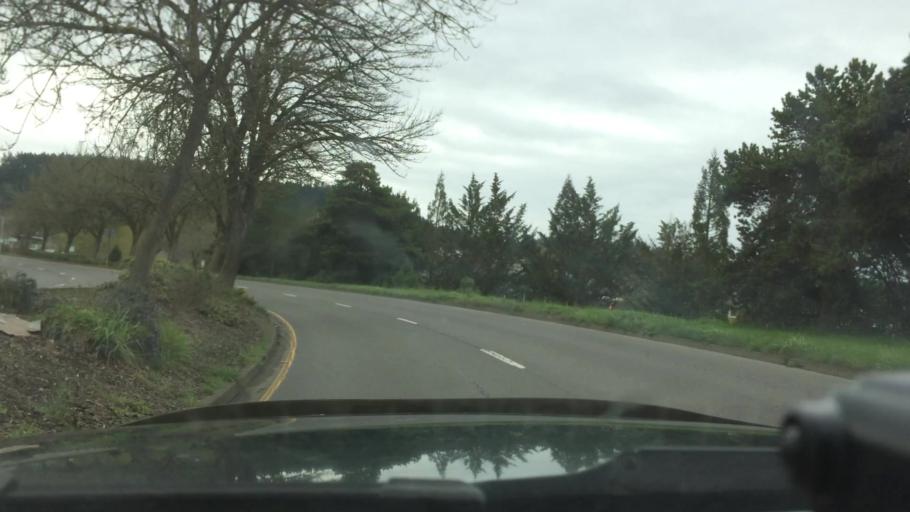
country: US
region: Oregon
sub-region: Lane County
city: Eugene
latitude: 44.0249
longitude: -123.0842
